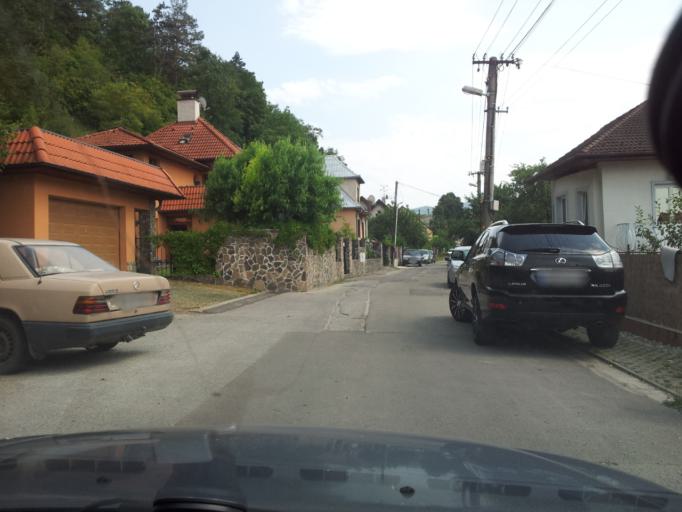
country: SK
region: Trenciansky
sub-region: Okres Trencin
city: Trencin
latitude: 48.8936
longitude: 18.0874
